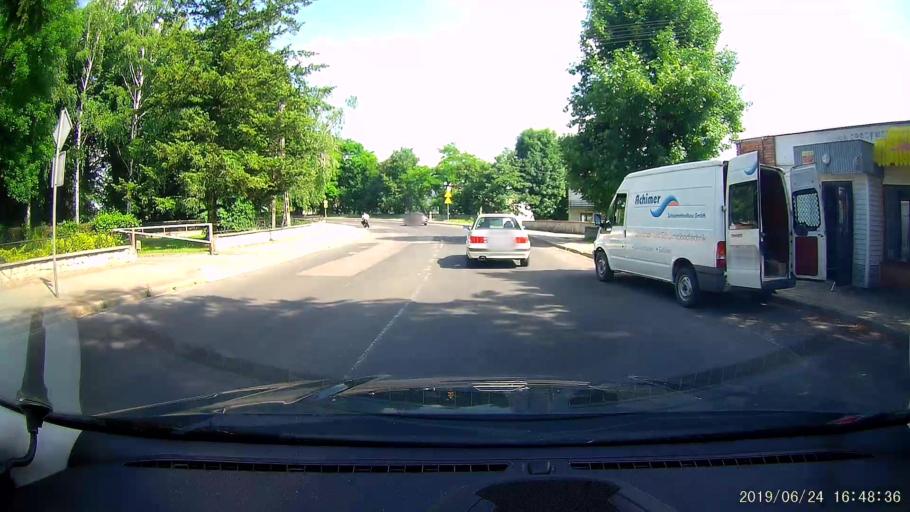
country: PL
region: Lublin Voivodeship
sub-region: Powiat tomaszowski
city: Laszczow
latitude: 50.5313
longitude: 23.7163
